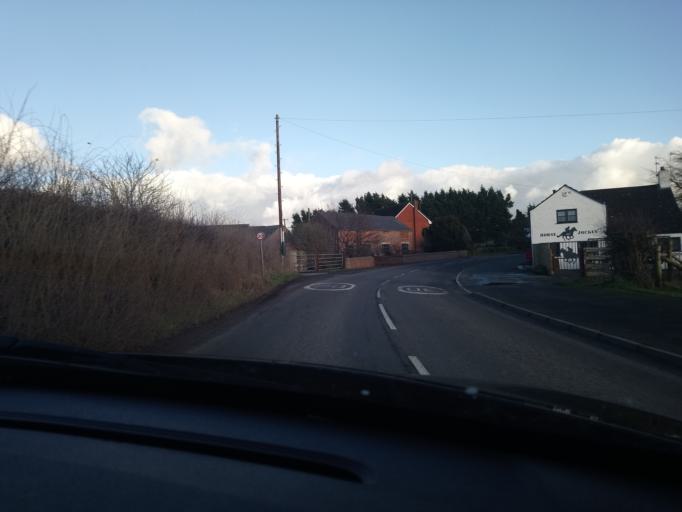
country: GB
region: England
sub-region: Shropshire
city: Petton
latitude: 52.8949
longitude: -2.7980
